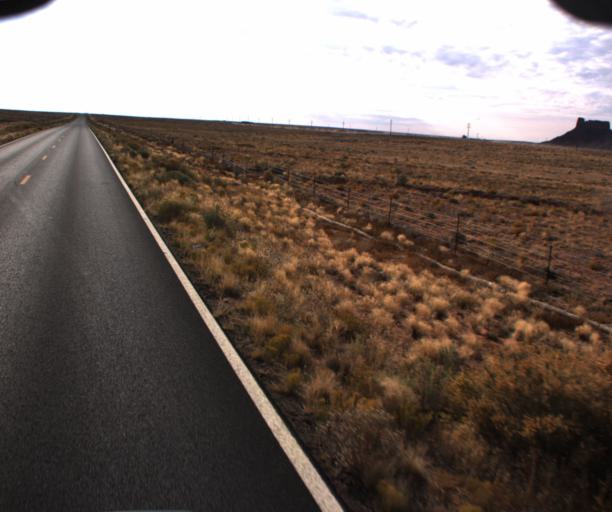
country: US
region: Arizona
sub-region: Apache County
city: Many Farms
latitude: 36.5605
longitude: -109.5396
